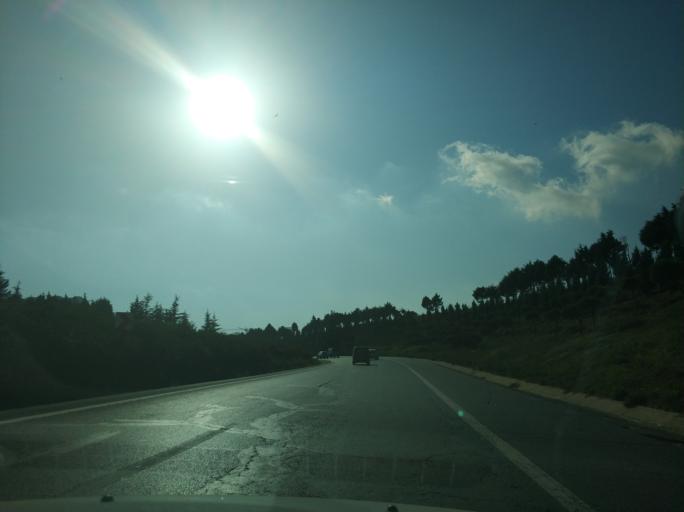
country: TR
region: Istanbul
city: Sultangazi
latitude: 41.0922
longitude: 28.9125
